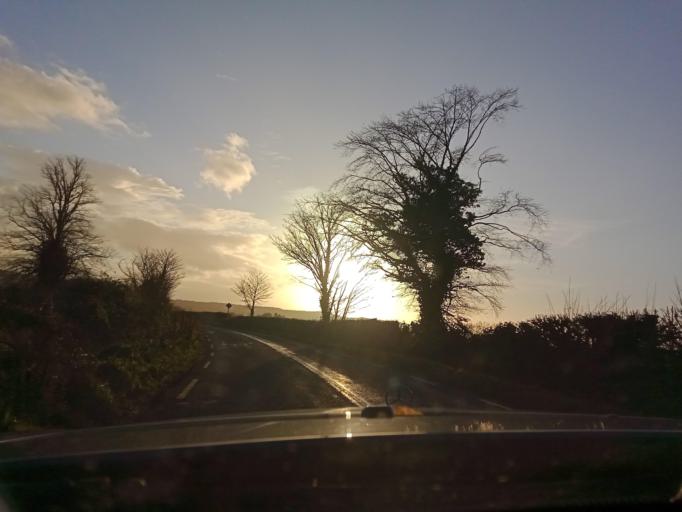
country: IE
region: Leinster
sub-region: Kilkenny
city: Callan
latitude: 52.4841
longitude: -7.3254
